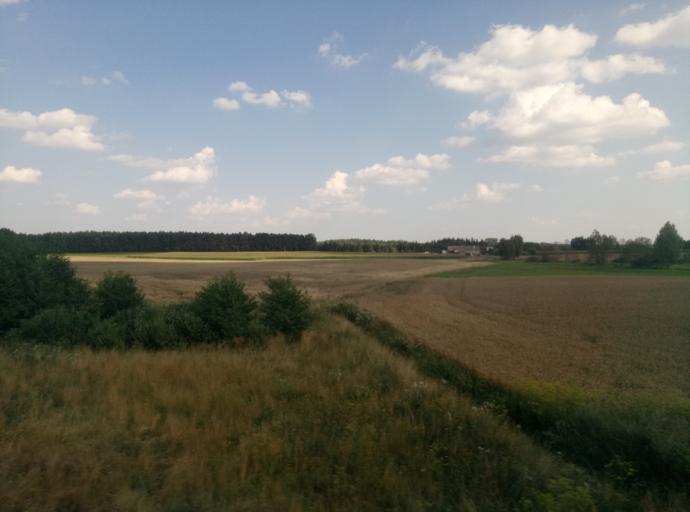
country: PL
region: Kujawsko-Pomorskie
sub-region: Powiat wabrzeski
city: Wabrzezno
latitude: 53.2453
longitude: 18.9643
